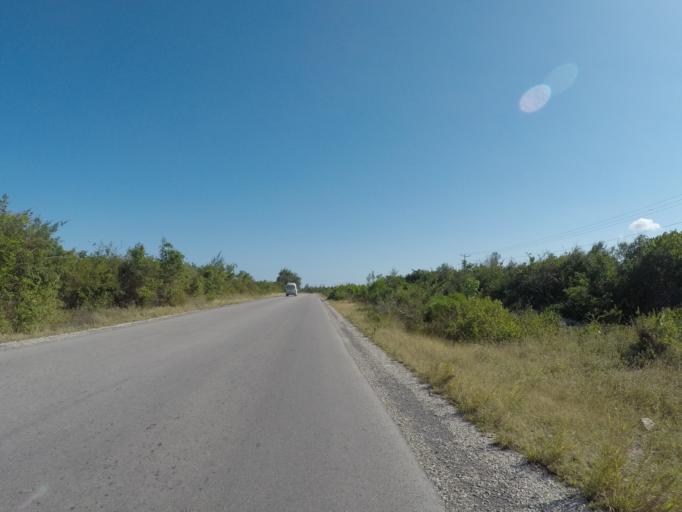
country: TZ
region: Zanzibar Central/South
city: Nganane
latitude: -6.2106
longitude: 39.5305
